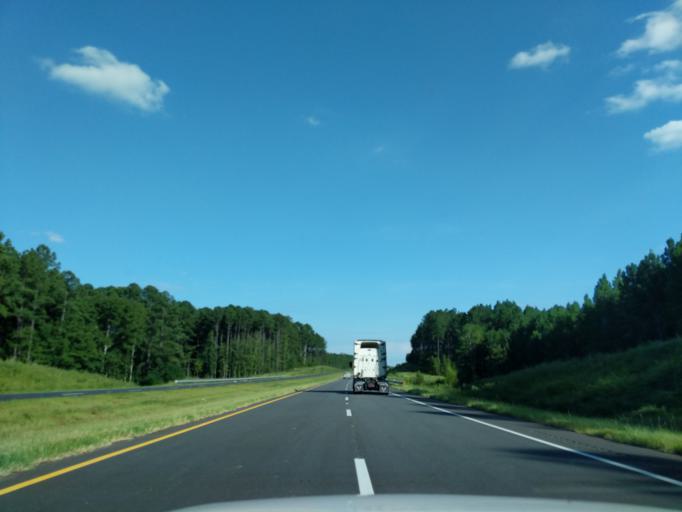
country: US
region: Georgia
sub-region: Wilkes County
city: Washington
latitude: 33.6920
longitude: -82.6494
